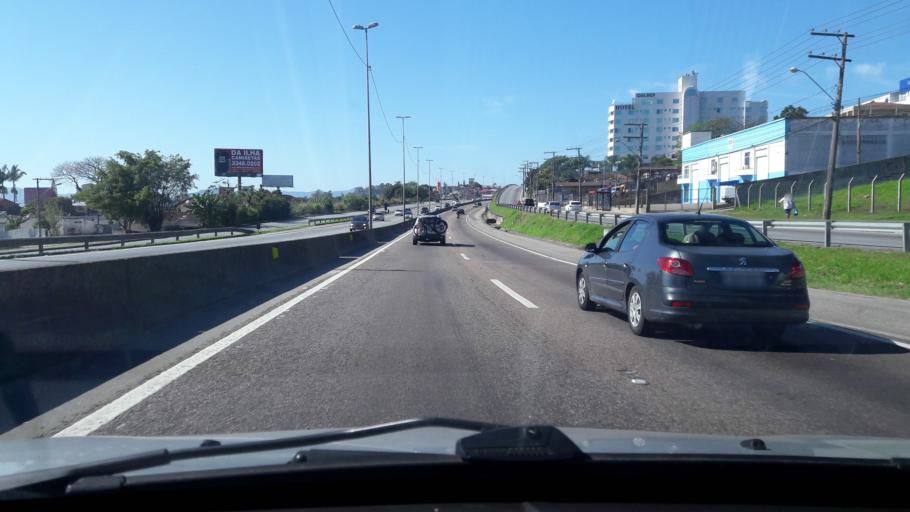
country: BR
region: Santa Catarina
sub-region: Biguacu
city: Biguacu
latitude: -27.5389
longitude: -48.6241
